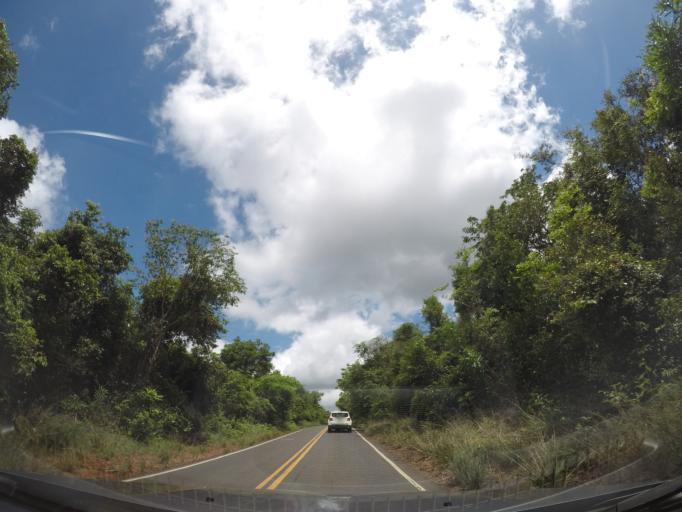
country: BR
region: Bahia
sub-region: Andarai
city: Vera Cruz
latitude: -12.5031
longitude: -41.3628
